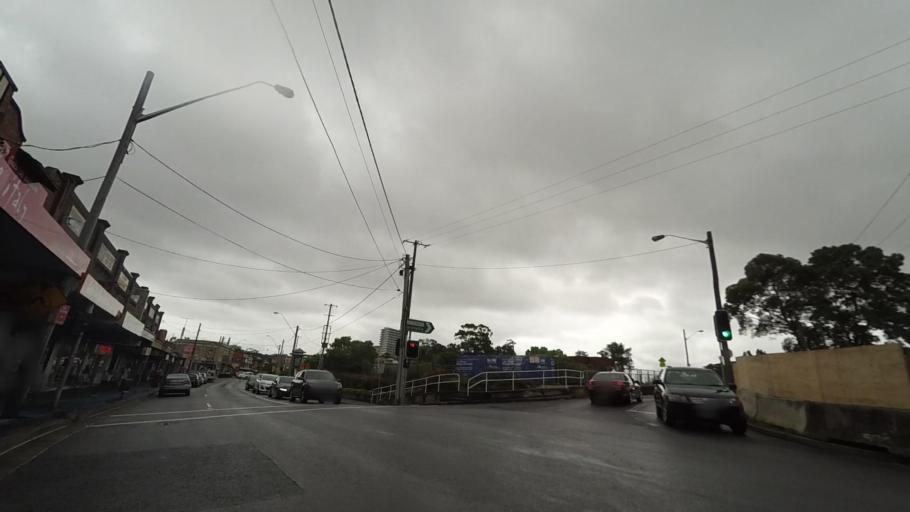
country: AU
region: New South Wales
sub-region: Kogarah
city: Kogarah Bay
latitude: -33.9702
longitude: 151.1159
